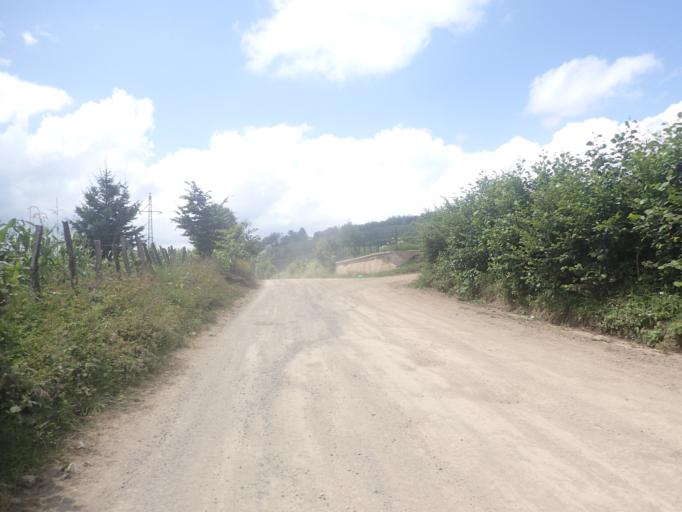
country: TR
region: Ordu
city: Aybasti
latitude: 40.7259
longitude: 37.3477
